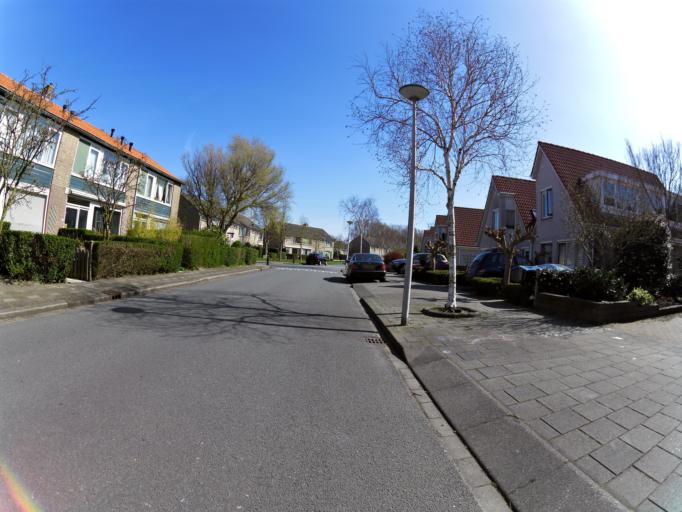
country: NL
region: South Holland
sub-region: Gemeente Brielle
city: Brielle
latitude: 51.9102
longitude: 4.1019
